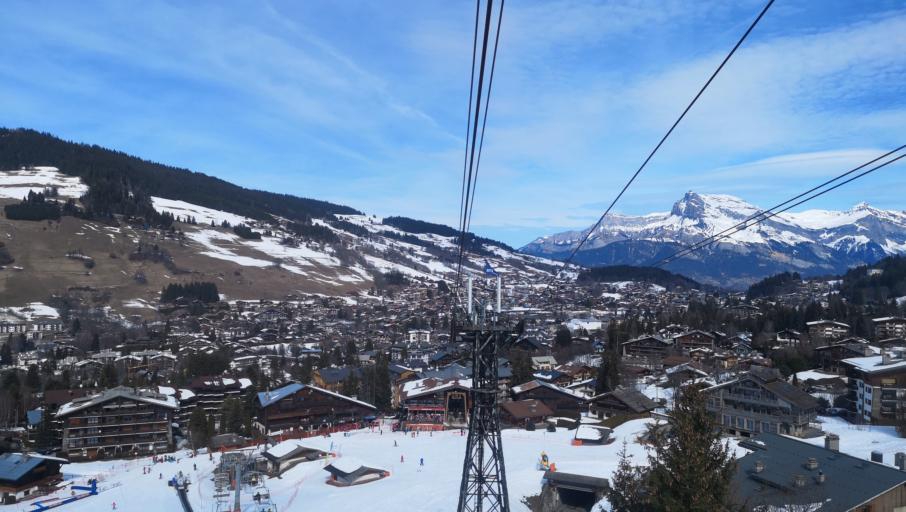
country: FR
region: Rhone-Alpes
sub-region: Departement de la Haute-Savoie
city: Megeve
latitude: 45.8475
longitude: 6.6150
